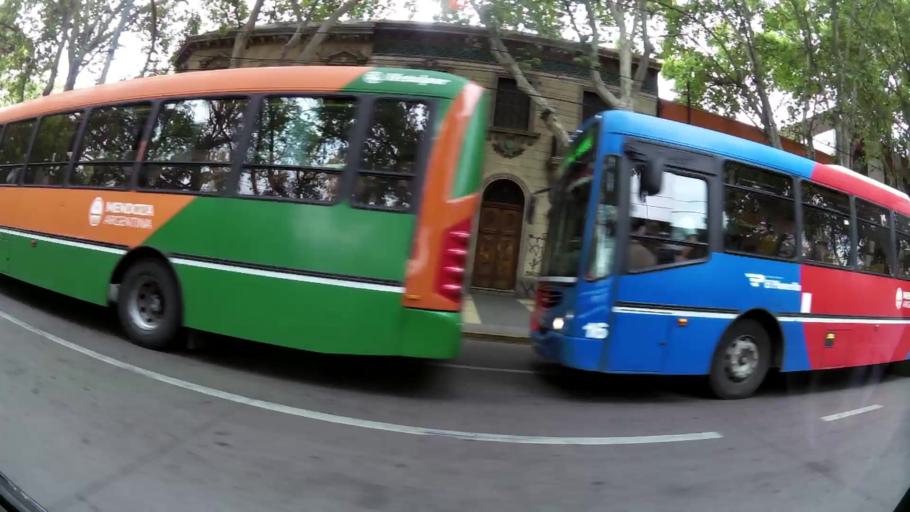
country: AR
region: Mendoza
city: Mendoza
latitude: -32.8834
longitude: -68.8420
